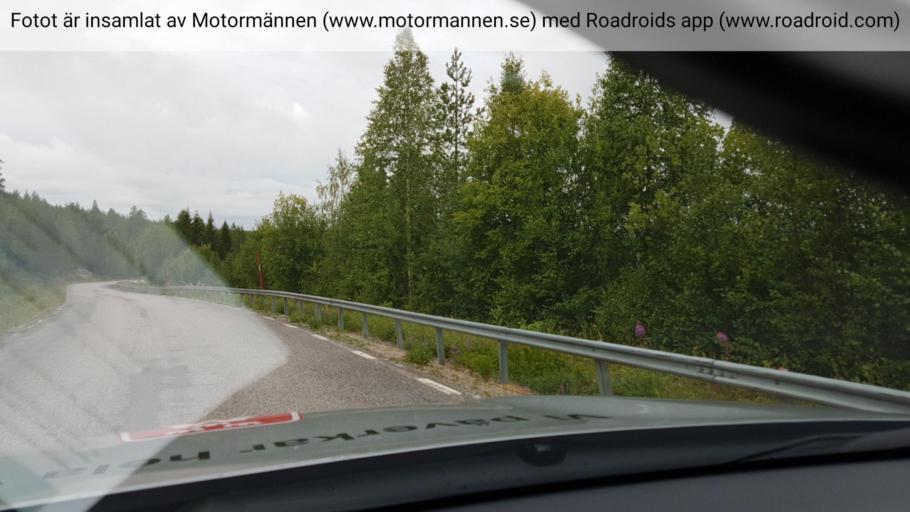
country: SE
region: Norrbotten
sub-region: Bodens Kommun
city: Saevast
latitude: 65.6705
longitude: 21.6949
